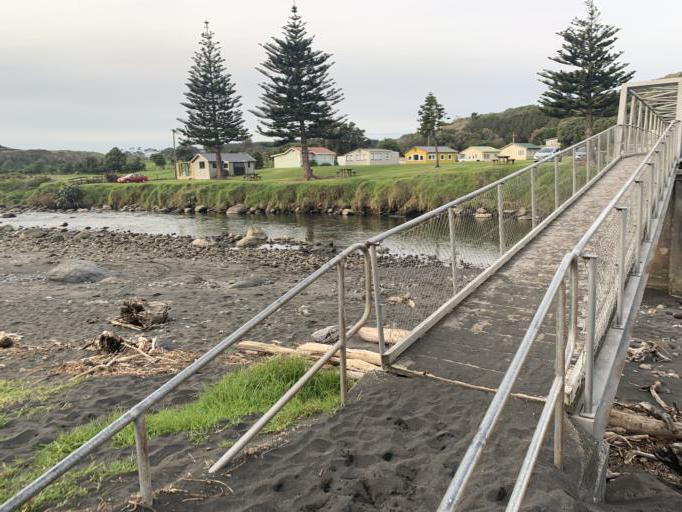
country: NZ
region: Taranaki
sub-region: South Taranaki District
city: Hawera
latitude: -39.5654
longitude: 174.0608
